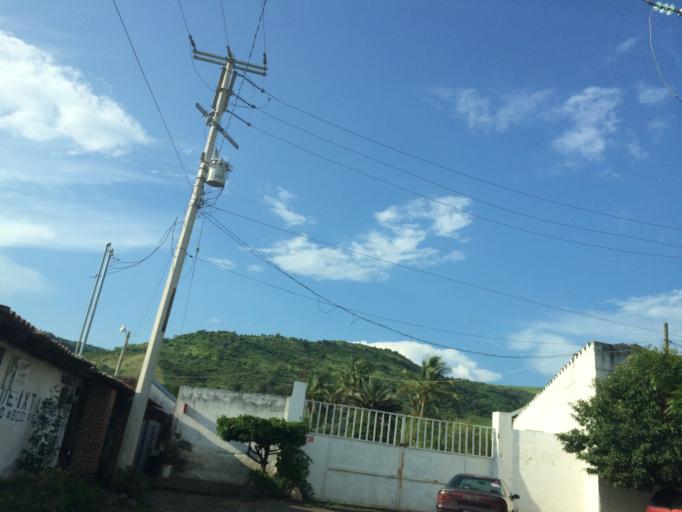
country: MX
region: Nayarit
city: Ixtlan del Rio
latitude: 21.0358
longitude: -104.3884
